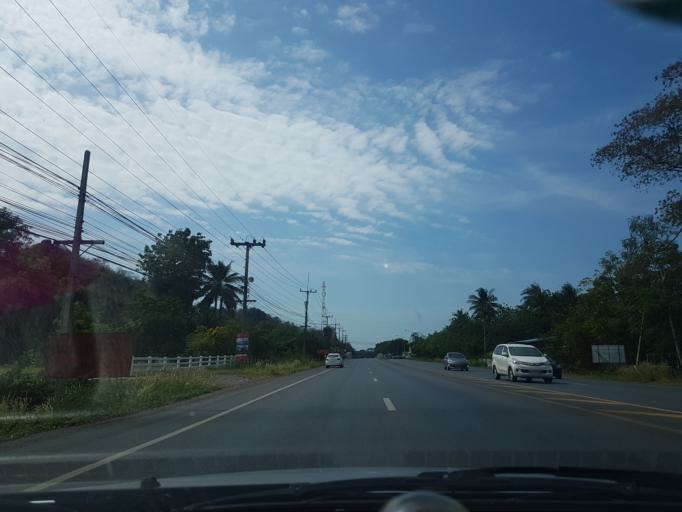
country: TH
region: Sara Buri
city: Phra Phutthabat
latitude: 14.8061
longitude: 100.7680
